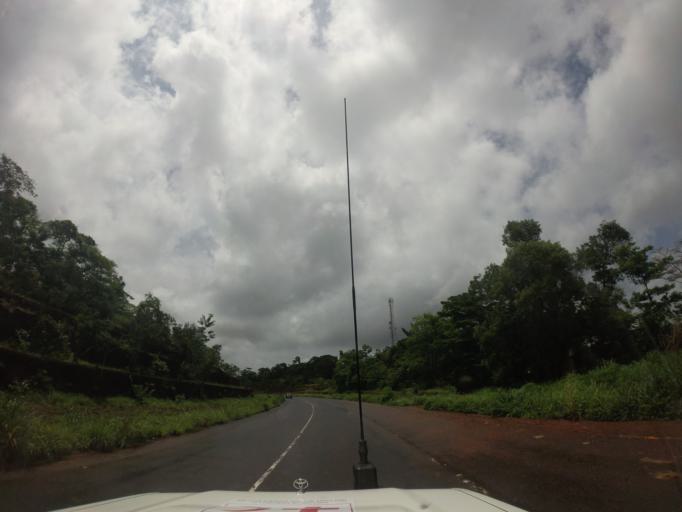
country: SL
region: Northern Province
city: Pepel
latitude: 8.4611
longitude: -12.8365
